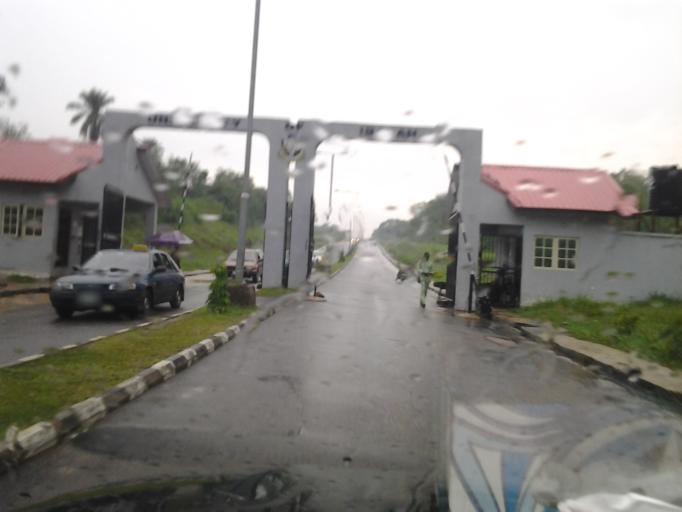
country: NG
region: Oyo
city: Moniya
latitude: 7.4598
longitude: 3.8988
